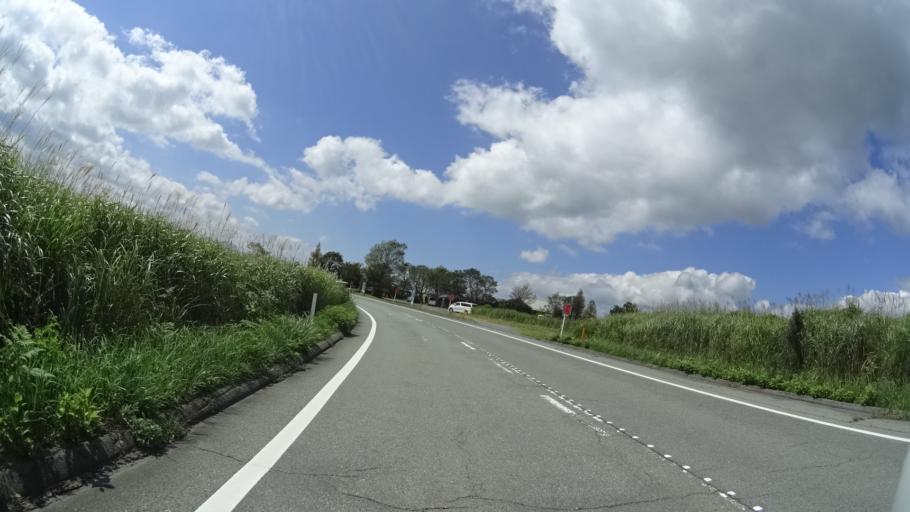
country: JP
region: Kumamoto
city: Aso
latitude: 33.0236
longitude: 131.1516
